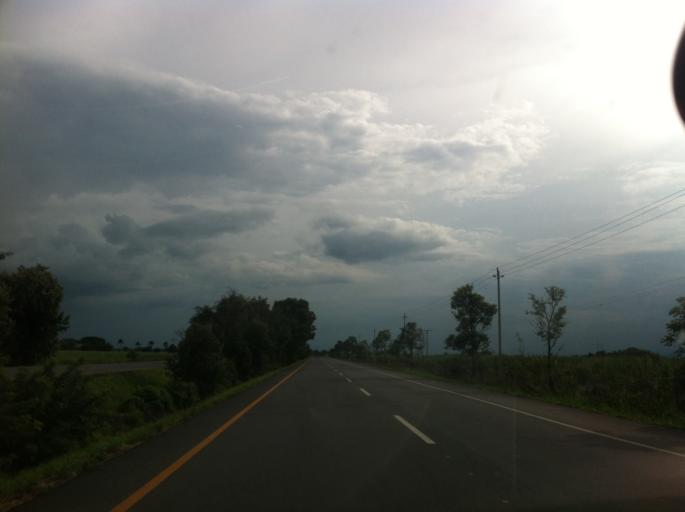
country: CO
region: Valle del Cauca
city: Palmira
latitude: 3.5547
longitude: -76.3368
